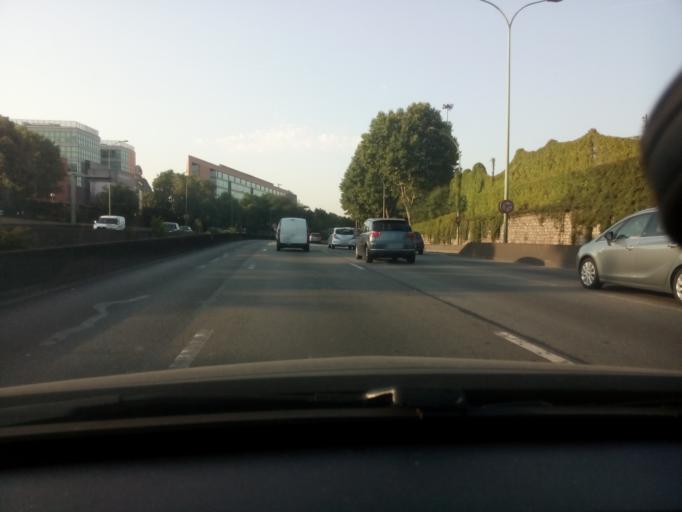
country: FR
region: Ile-de-France
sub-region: Departement du Val-de-Marne
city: Saint-Mande
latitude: 48.8526
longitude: 2.4145
